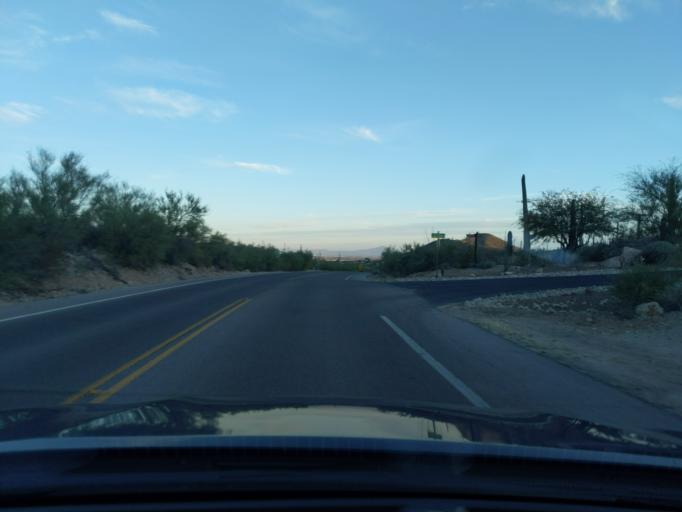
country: US
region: Arizona
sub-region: Pima County
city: Tucson Estates
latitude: 32.2285
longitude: -111.0403
